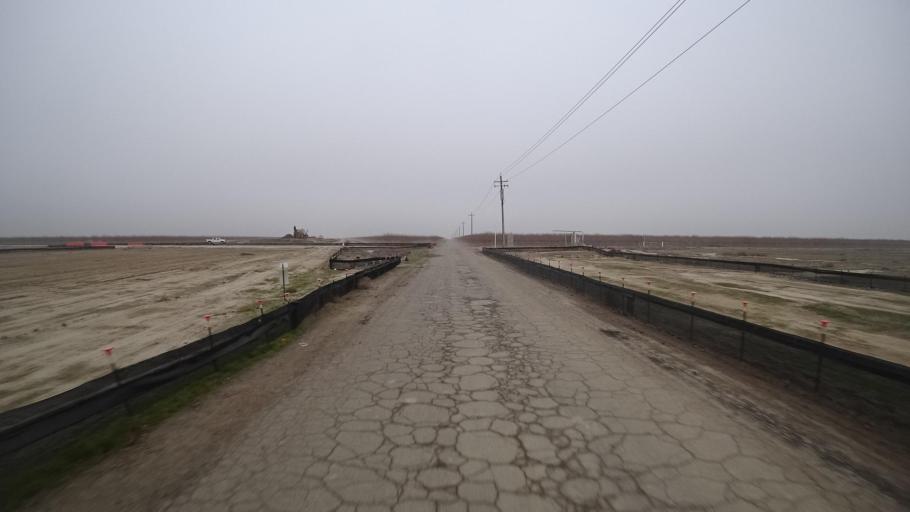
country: US
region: California
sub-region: Tulare County
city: Alpaugh
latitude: 35.7764
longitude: -119.4011
